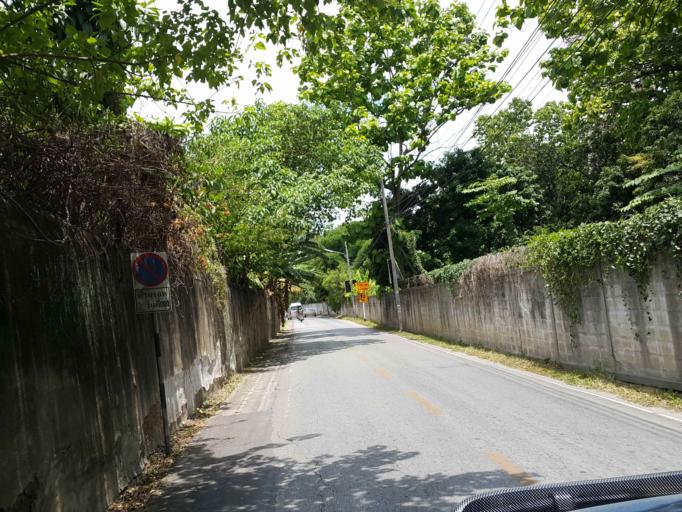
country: TH
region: Chiang Mai
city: Chiang Mai
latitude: 18.7793
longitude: 99.0155
